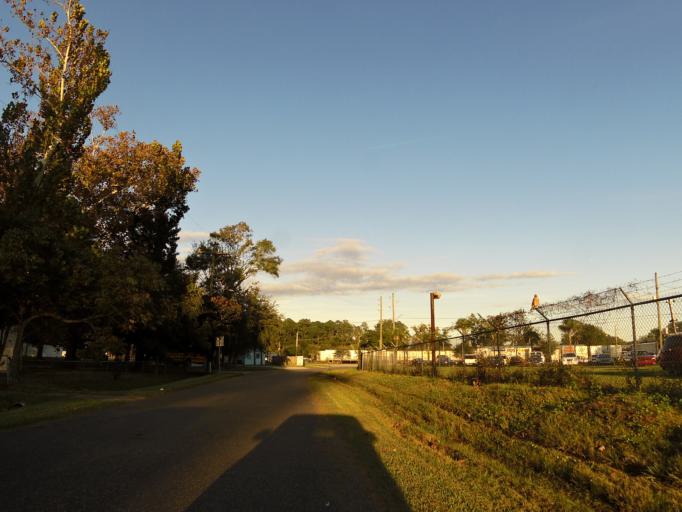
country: US
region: Florida
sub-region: Duval County
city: Jacksonville
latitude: 30.3572
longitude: -81.7323
